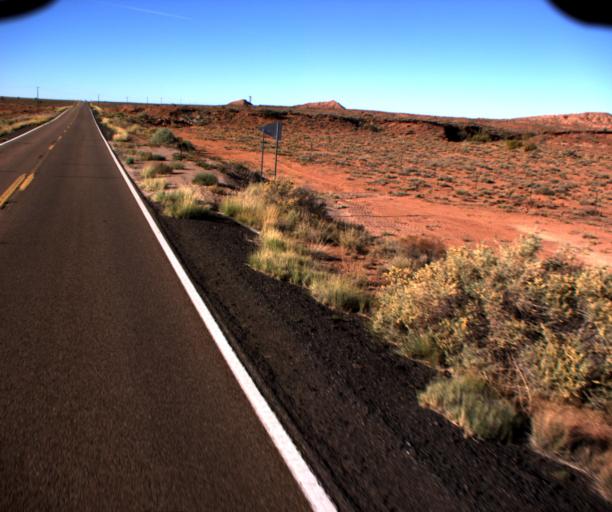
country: US
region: Arizona
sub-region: Navajo County
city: Holbrook
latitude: 34.8561
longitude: -110.1699
